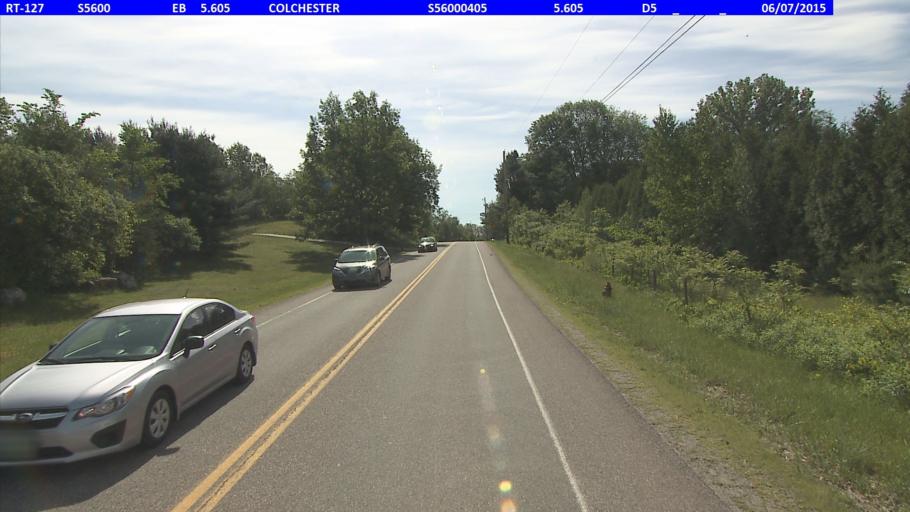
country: US
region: Vermont
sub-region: Chittenden County
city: Colchester
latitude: 44.5311
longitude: -73.1775
